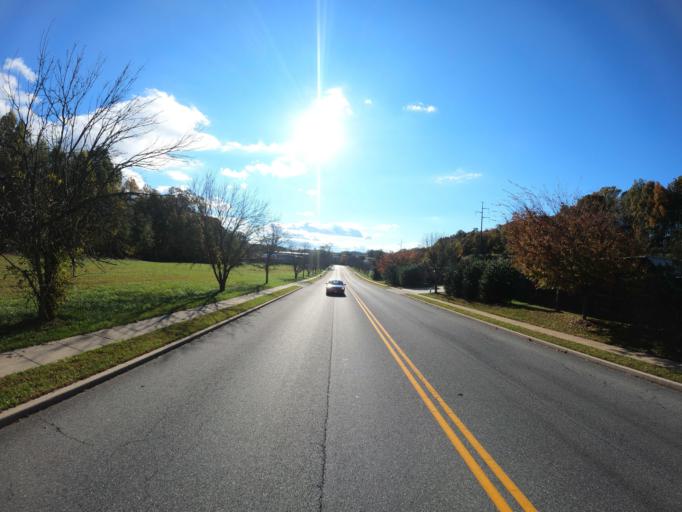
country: US
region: Maryland
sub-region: Carroll County
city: Mount Airy
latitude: 39.3715
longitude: -77.1692
